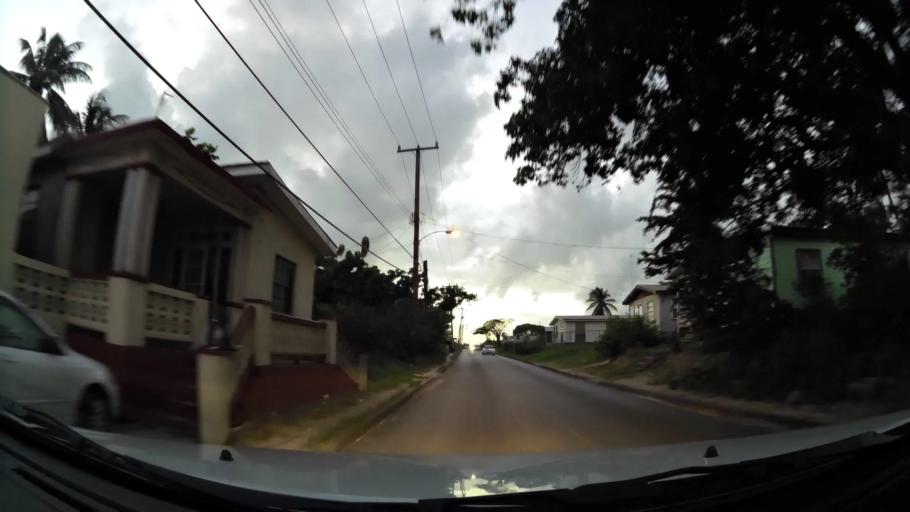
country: BB
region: Saint Philip
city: Crane
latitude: 13.1184
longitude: -59.4821
